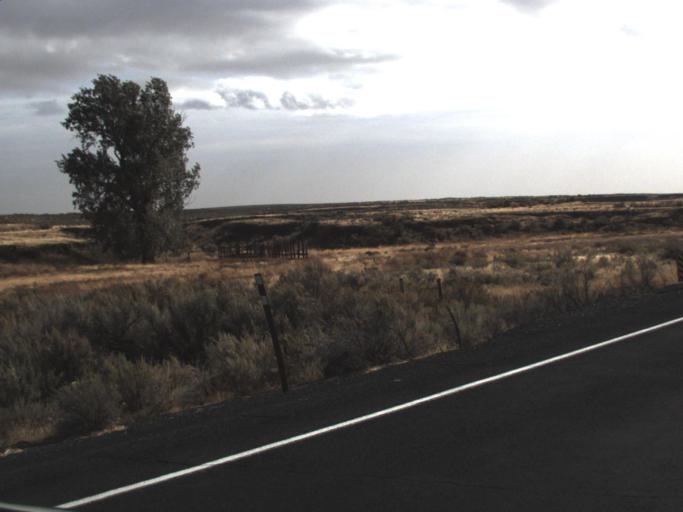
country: US
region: Washington
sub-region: Okanogan County
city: Coulee Dam
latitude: 47.5315
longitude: -118.7823
